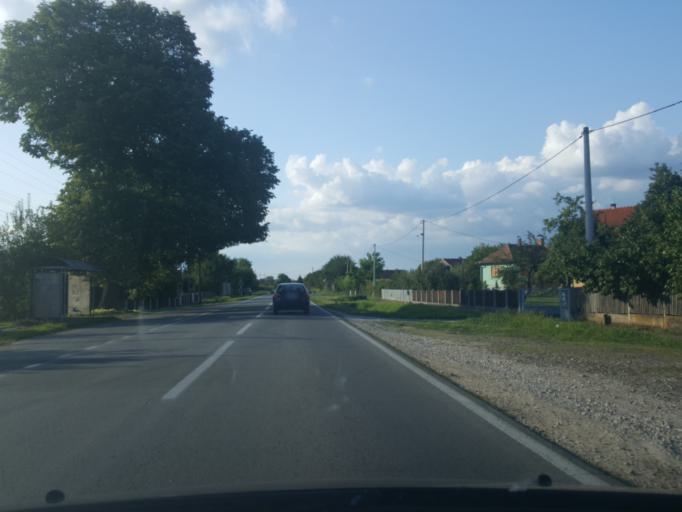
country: RS
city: Lipnicki Sor
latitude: 44.5933
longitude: 19.2578
